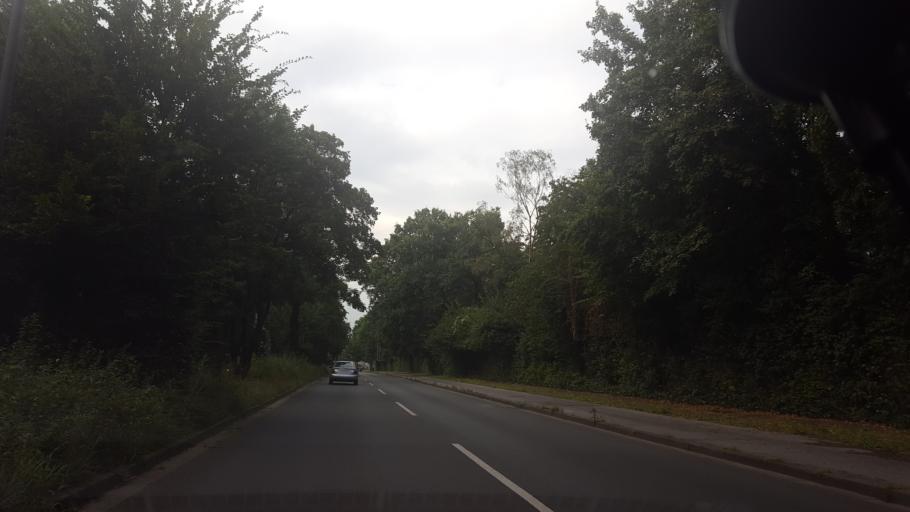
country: DE
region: North Rhine-Westphalia
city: Marl
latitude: 51.6699
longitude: 7.1033
